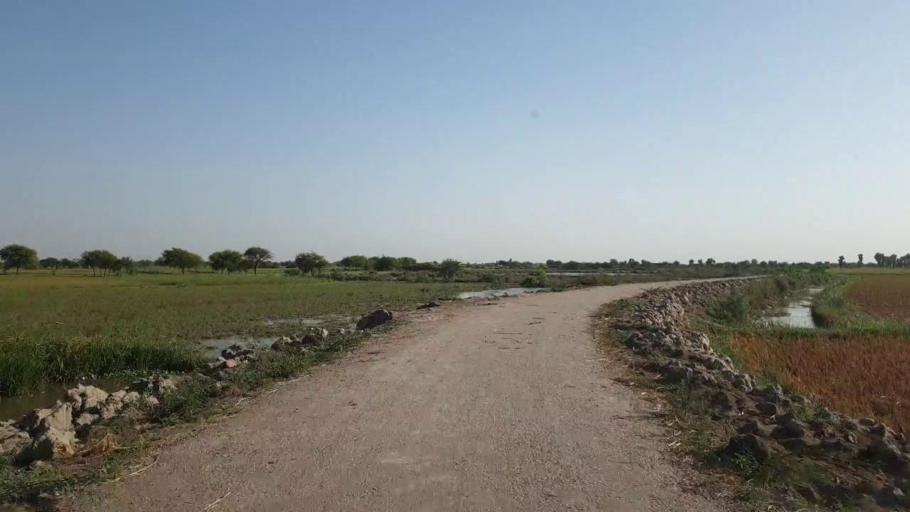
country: PK
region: Sindh
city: Badin
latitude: 24.5968
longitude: 68.9111
